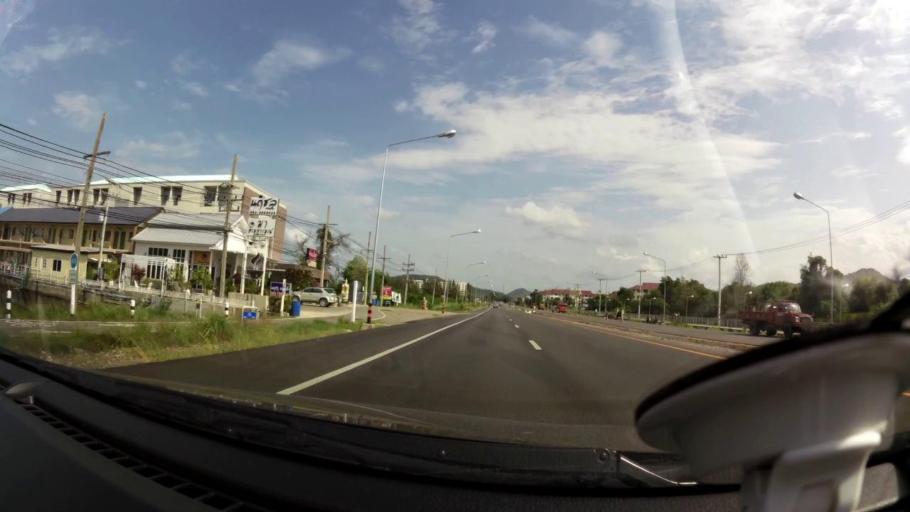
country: TH
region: Prachuap Khiri Khan
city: Hua Hin
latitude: 12.4785
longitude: 99.9715
